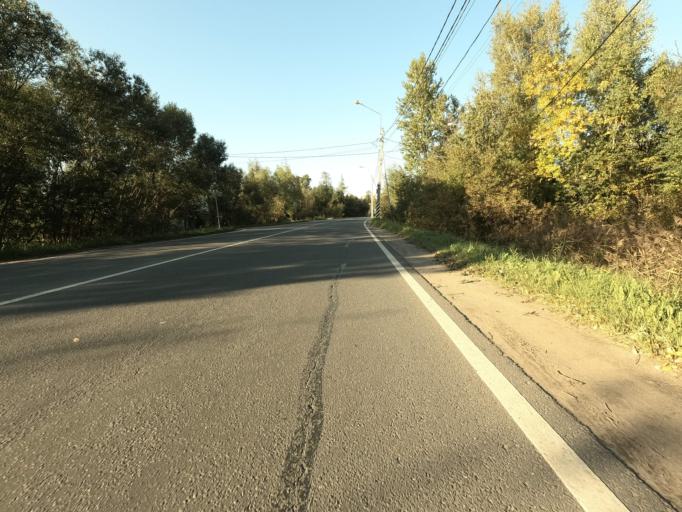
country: RU
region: St.-Petersburg
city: Kolpino
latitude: 59.7538
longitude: 30.6158
